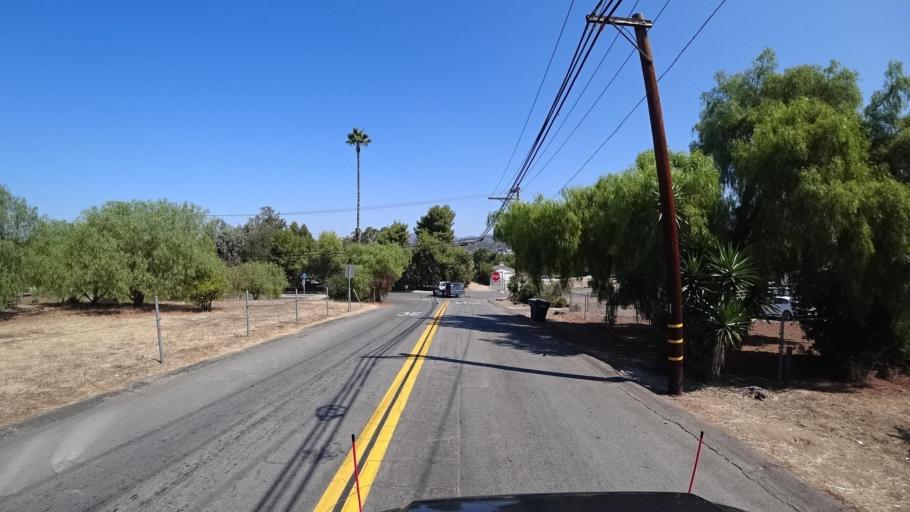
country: US
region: California
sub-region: San Diego County
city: Lake San Marcos
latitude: 33.1526
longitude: -117.2074
